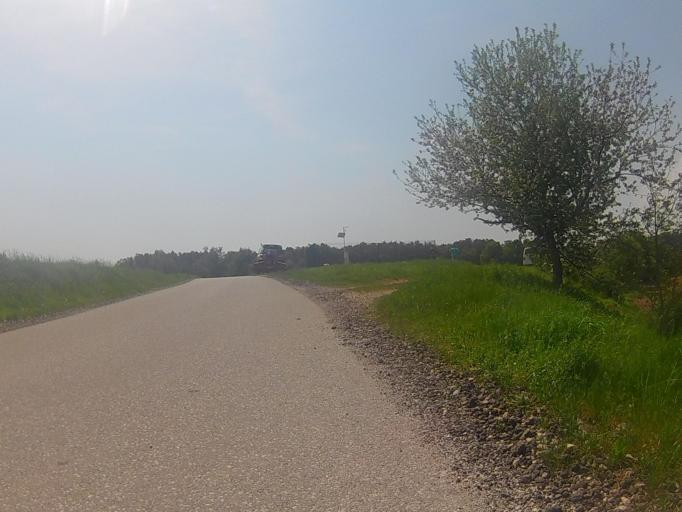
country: SI
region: Starse
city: Starse
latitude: 46.4633
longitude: 15.7576
